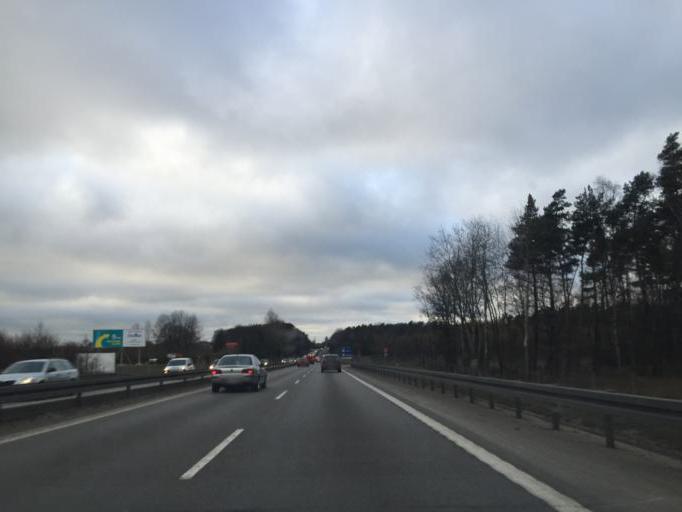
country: PL
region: Pomeranian Voivodeship
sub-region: Sopot
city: Sopot
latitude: 54.3857
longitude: 18.5017
